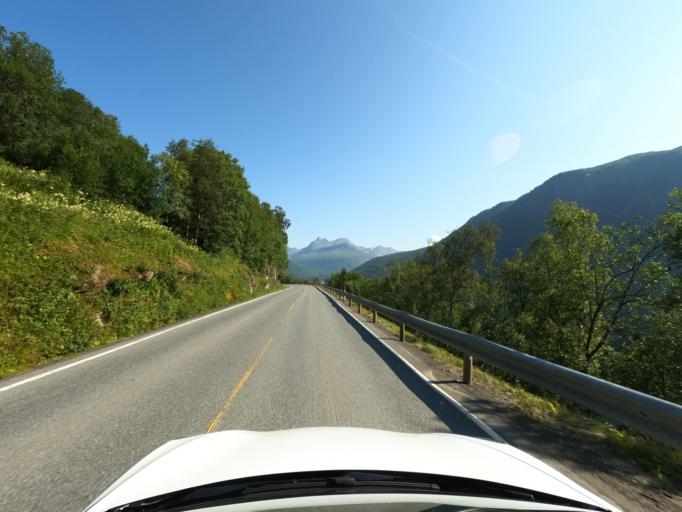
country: NO
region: Nordland
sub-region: Narvik
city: Narvik
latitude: 68.3914
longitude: 17.5396
